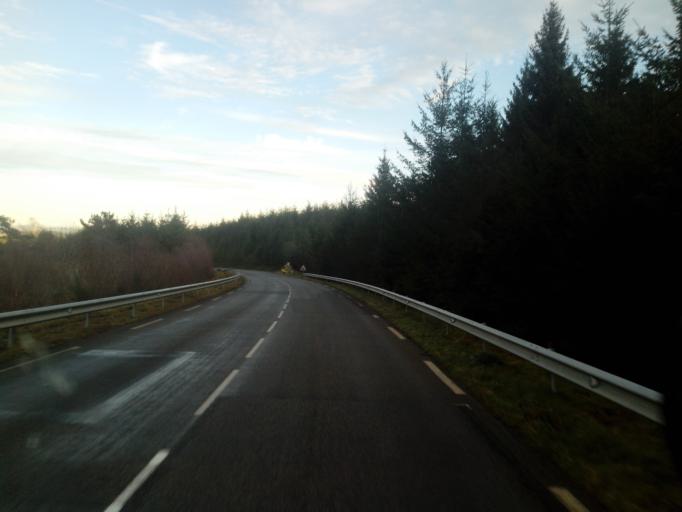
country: FR
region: Limousin
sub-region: Departement de la Correze
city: Meymac
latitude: 45.5777
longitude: 2.1090
